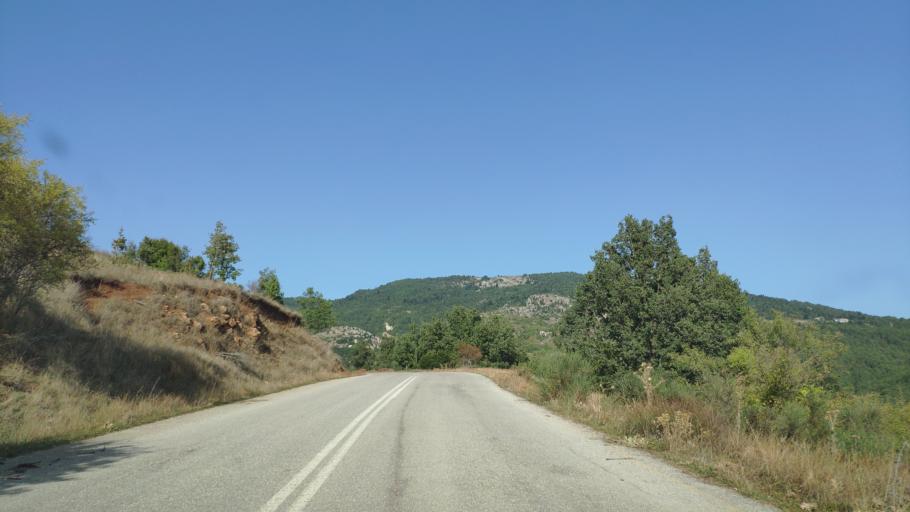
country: GR
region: West Greece
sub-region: Nomos Achaias
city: Aiyira
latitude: 38.0074
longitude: 22.4003
